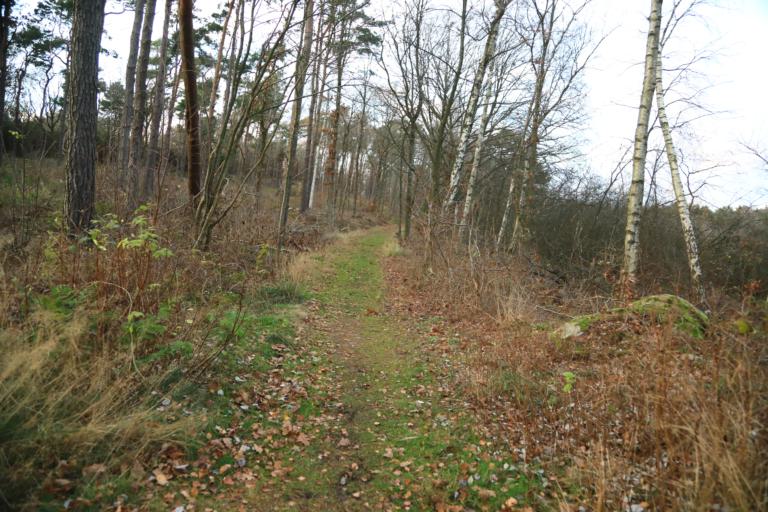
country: SE
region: Halland
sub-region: Varbergs Kommun
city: Varberg
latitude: 57.1442
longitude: 12.2228
